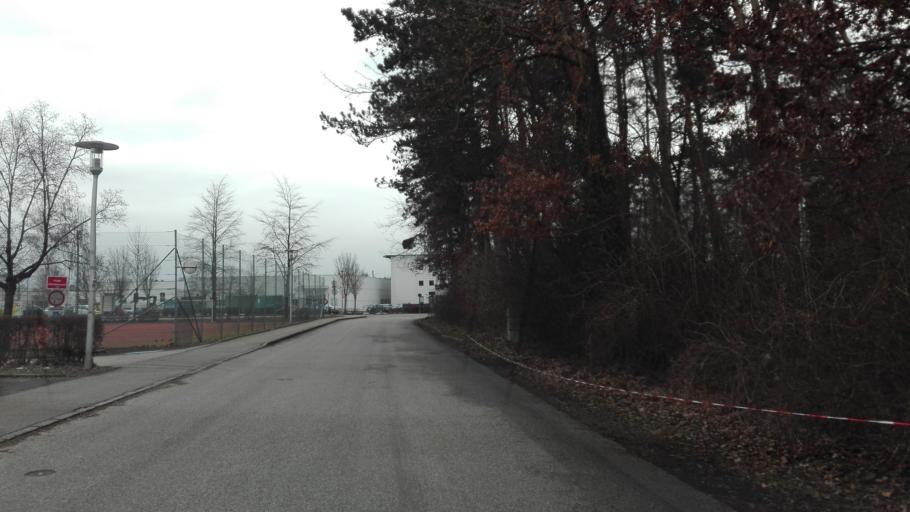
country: AT
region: Upper Austria
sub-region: Politischer Bezirk Linz-Land
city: Traun
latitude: 48.2355
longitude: 14.2267
